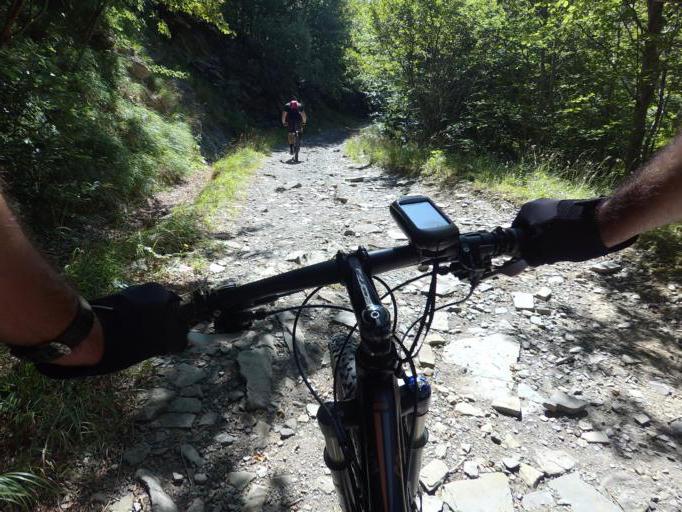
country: IT
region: Emilia-Romagna
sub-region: Provincia di Modena
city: Montecreto
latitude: 44.2285
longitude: 10.7288
